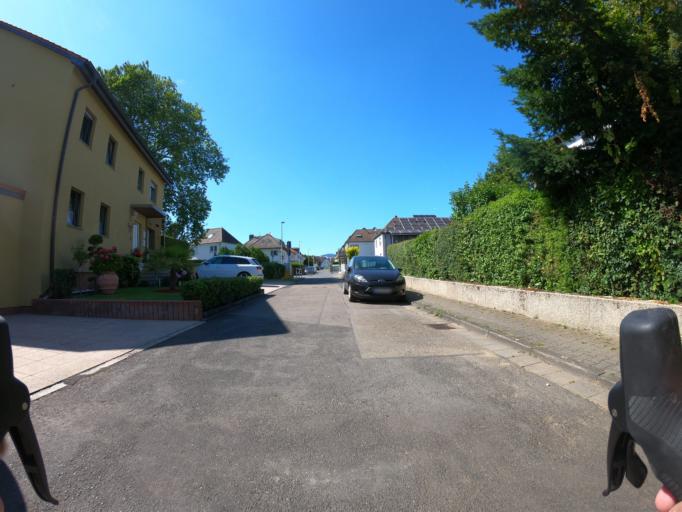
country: DE
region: Hesse
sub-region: Regierungsbezirk Darmstadt
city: Eschborn
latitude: 50.1409
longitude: 8.5581
